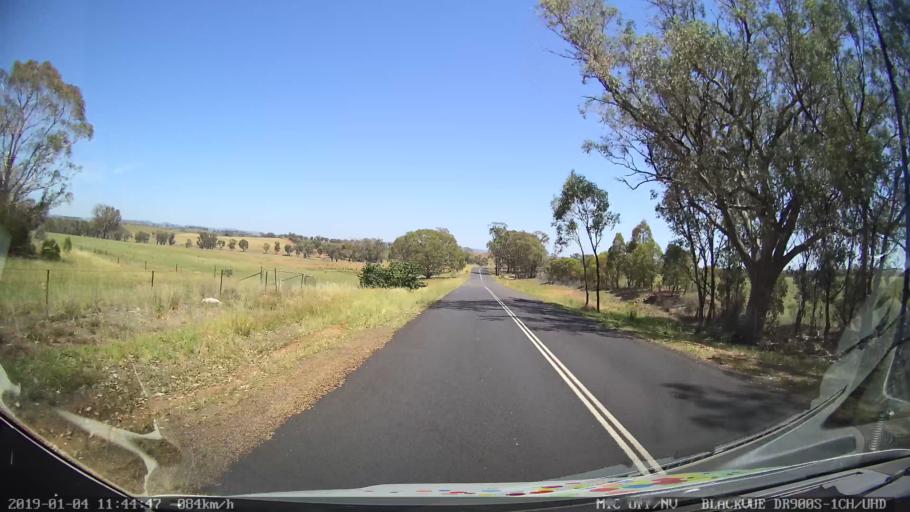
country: AU
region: New South Wales
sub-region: Cabonne
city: Molong
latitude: -32.9609
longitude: 148.7679
